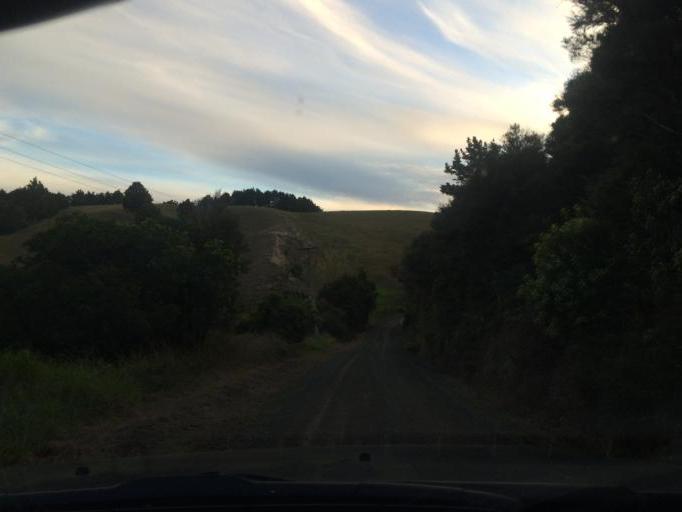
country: NZ
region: Northland
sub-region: Whangarei
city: Maungatapere
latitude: -35.8050
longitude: 174.0459
